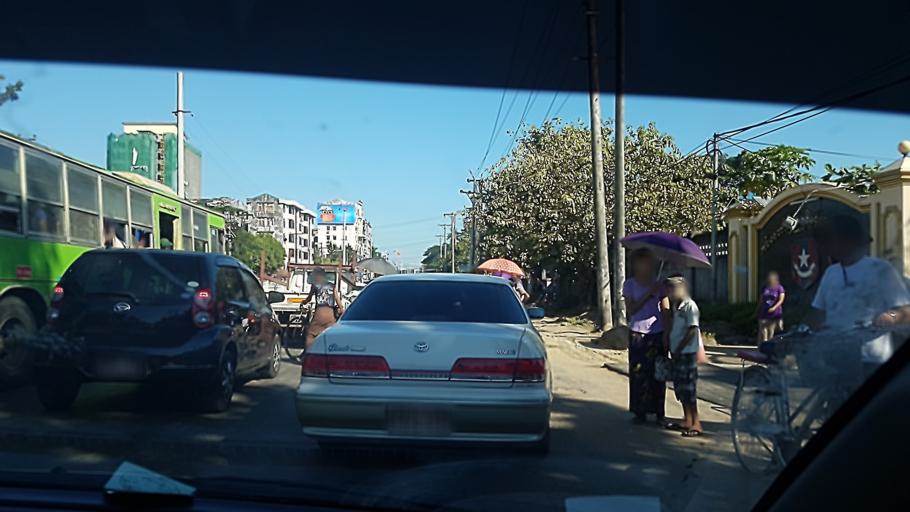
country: MM
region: Yangon
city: Yangon
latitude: 16.8558
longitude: 96.1238
